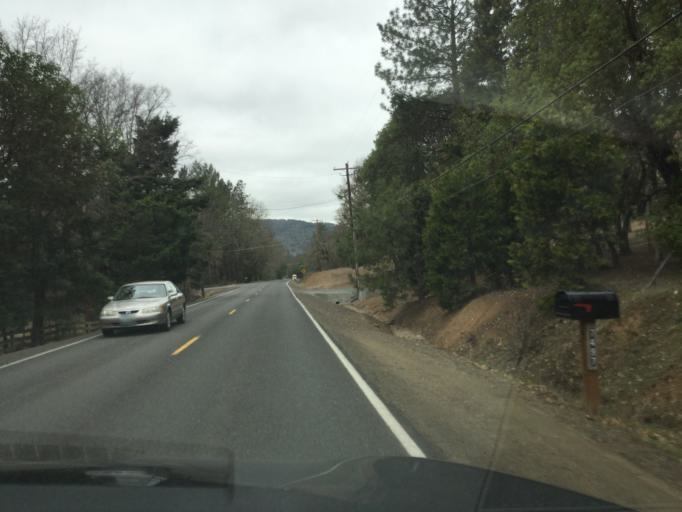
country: US
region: Oregon
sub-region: Jackson County
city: Gold Hill
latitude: 42.4000
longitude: -123.0217
